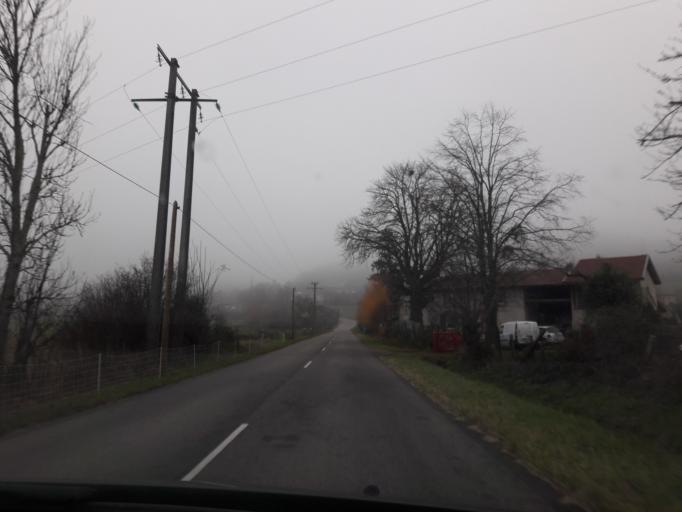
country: FR
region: Rhone-Alpes
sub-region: Departement de l'Isere
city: Chatonnay
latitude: 45.4245
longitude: 5.1859
